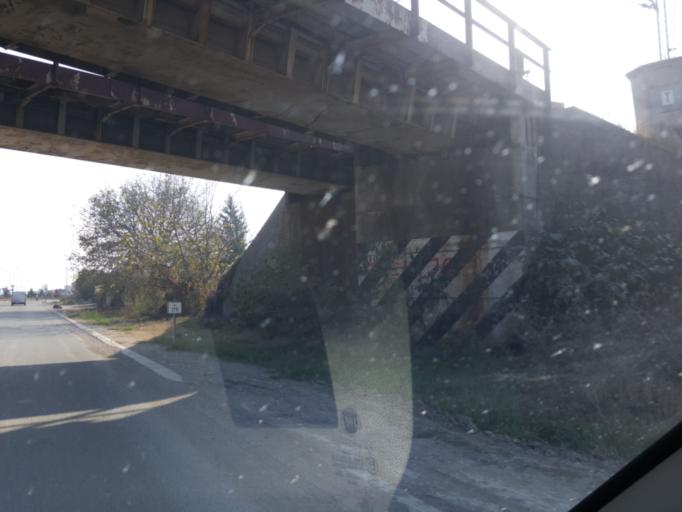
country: RS
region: Central Serbia
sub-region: Nisavski Okrug
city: Nis
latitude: 43.3197
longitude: 21.8281
